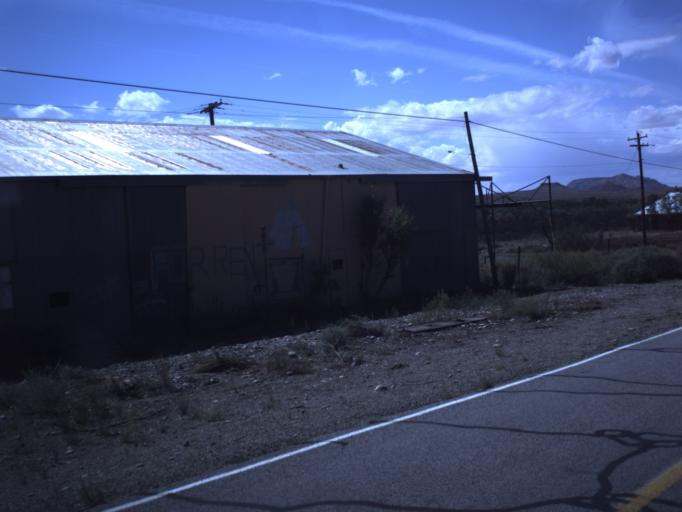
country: US
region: Utah
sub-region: San Juan County
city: Blanding
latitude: 37.2735
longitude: -109.3333
